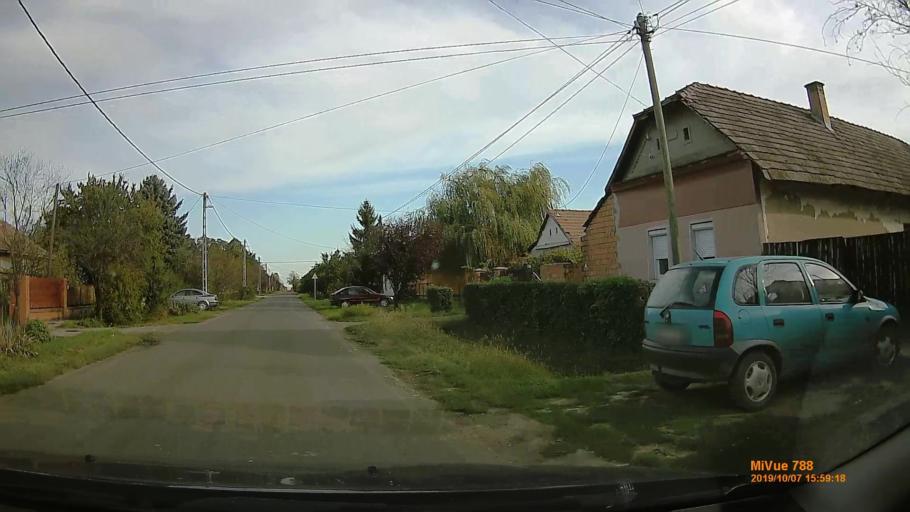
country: HU
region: Bekes
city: Szarvas
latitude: 46.8254
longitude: 20.6528
